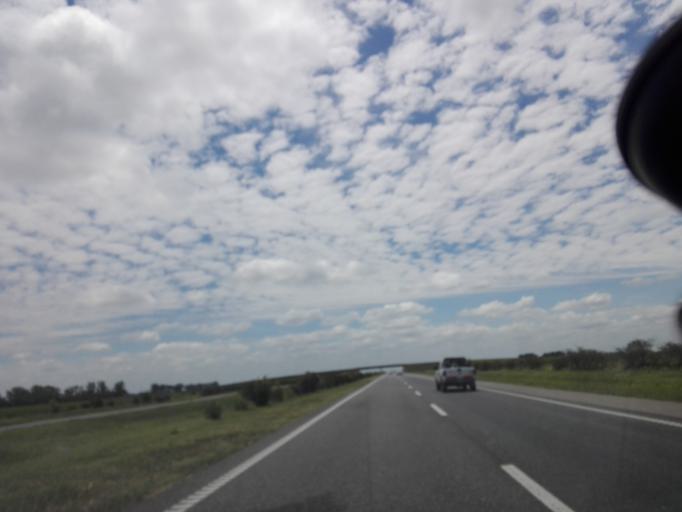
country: AR
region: Cordoba
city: Oliva
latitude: -31.9935
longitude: -63.5597
